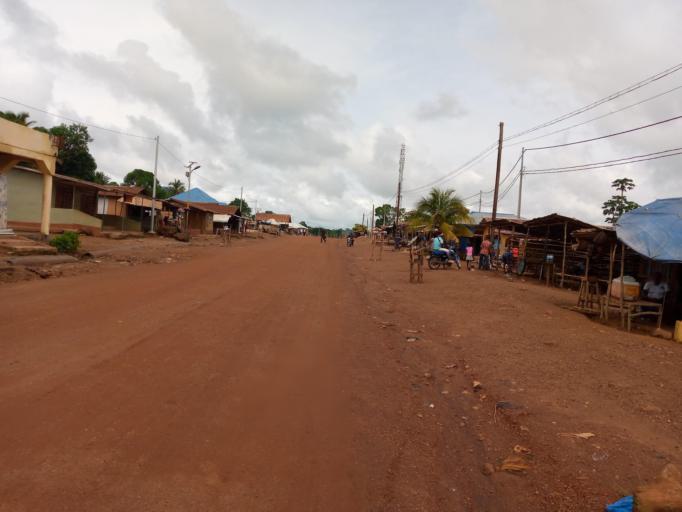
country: SL
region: Southern Province
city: Mogbwemo
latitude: 7.7619
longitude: -12.3066
